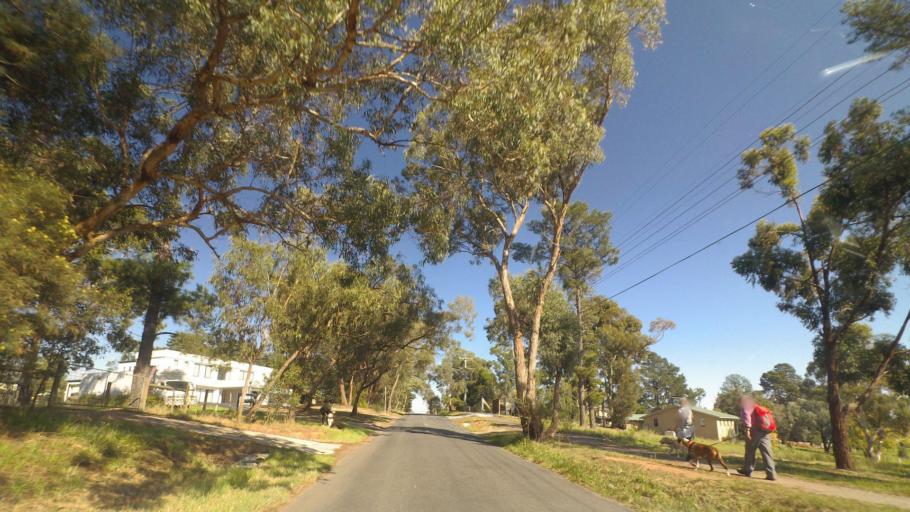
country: AU
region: Victoria
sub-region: Nillumbik
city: Eltham
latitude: -37.7509
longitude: 145.1544
